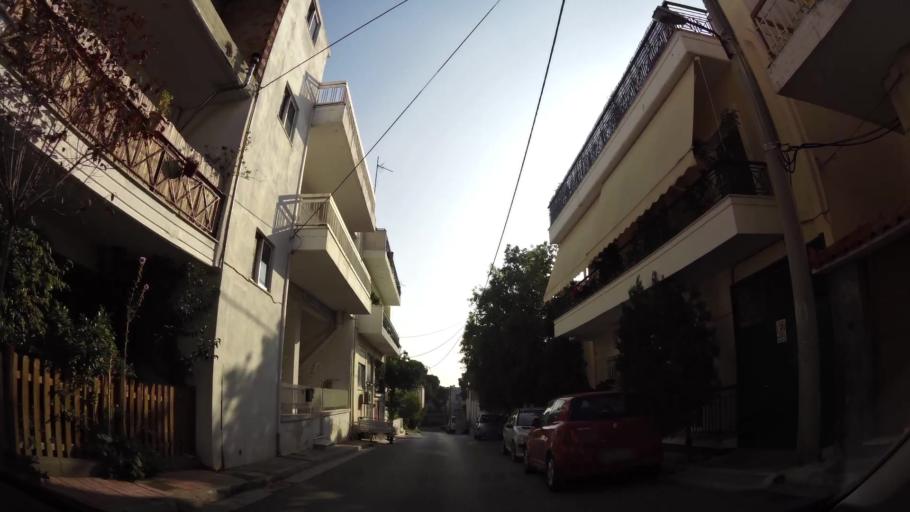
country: GR
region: Attica
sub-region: Nomarchia Dytikis Attikis
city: Zefyri
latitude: 38.0580
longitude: 23.7369
